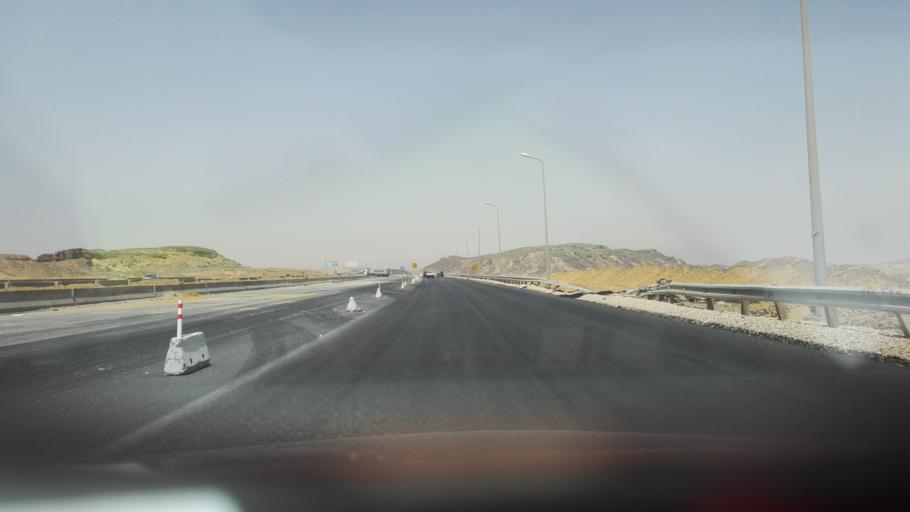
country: EG
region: As Suways
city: Ain Sukhna
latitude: 29.7083
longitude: 32.0845
